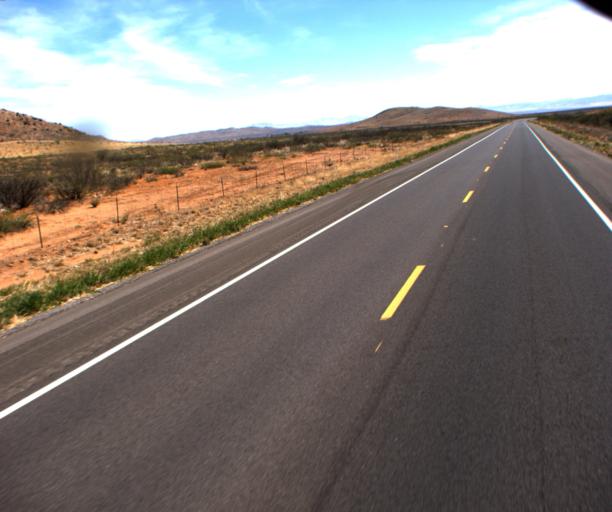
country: US
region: Arizona
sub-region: Cochise County
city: Tombstone
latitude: 31.9041
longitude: -109.7916
